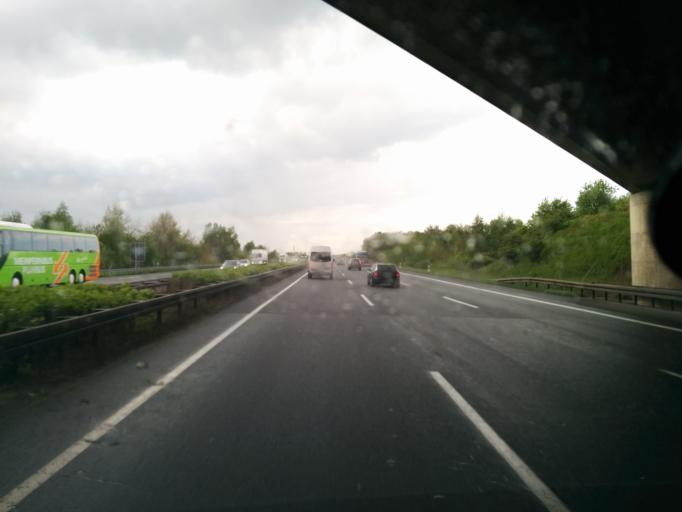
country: DE
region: Lower Saxony
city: Dollbergen
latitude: 52.3612
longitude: 10.1512
